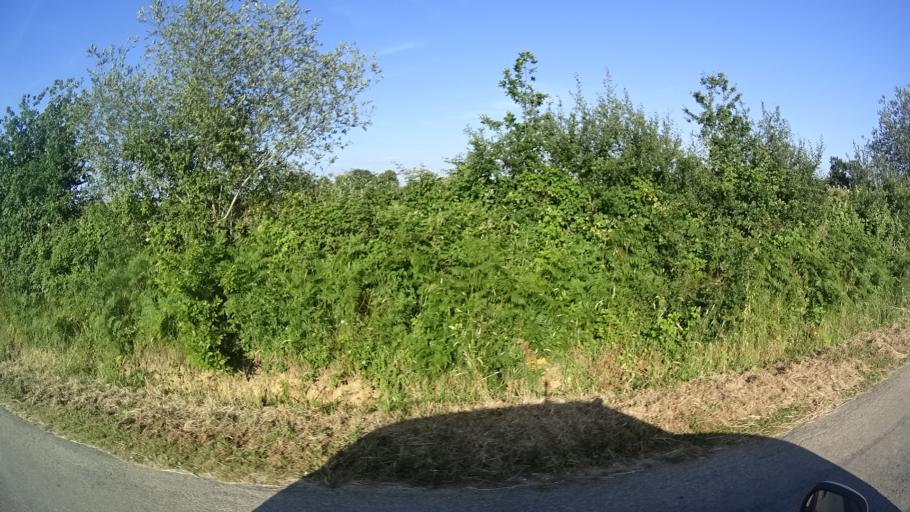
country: FR
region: Brittany
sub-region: Departement du Morbihan
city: Rieux
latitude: 47.5949
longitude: -2.1242
